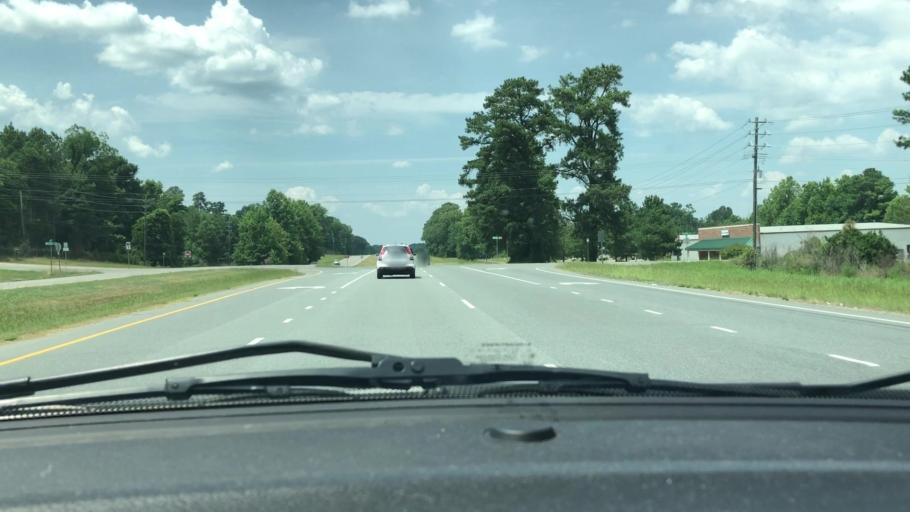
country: US
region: North Carolina
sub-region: Lee County
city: Sanford
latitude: 35.5031
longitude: -79.2061
